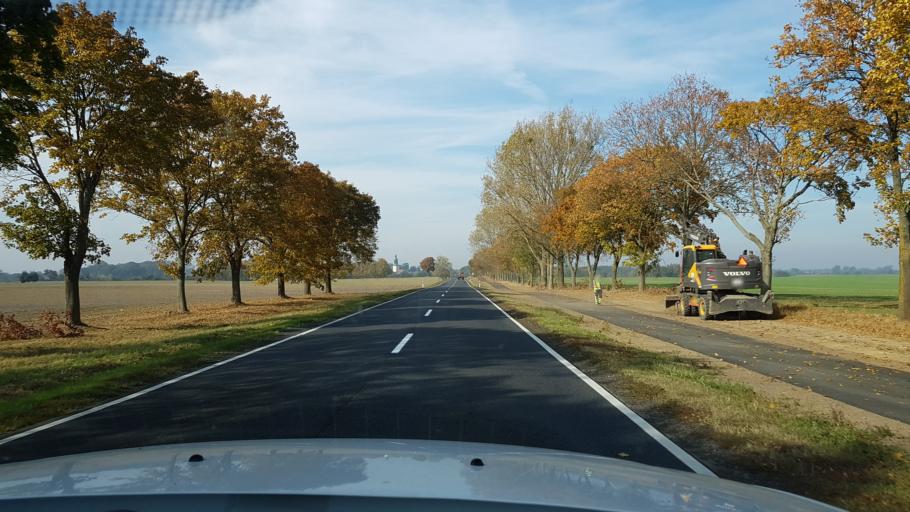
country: PL
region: West Pomeranian Voivodeship
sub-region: Powiat mysliborski
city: Mysliborz
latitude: 52.9424
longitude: 14.8062
